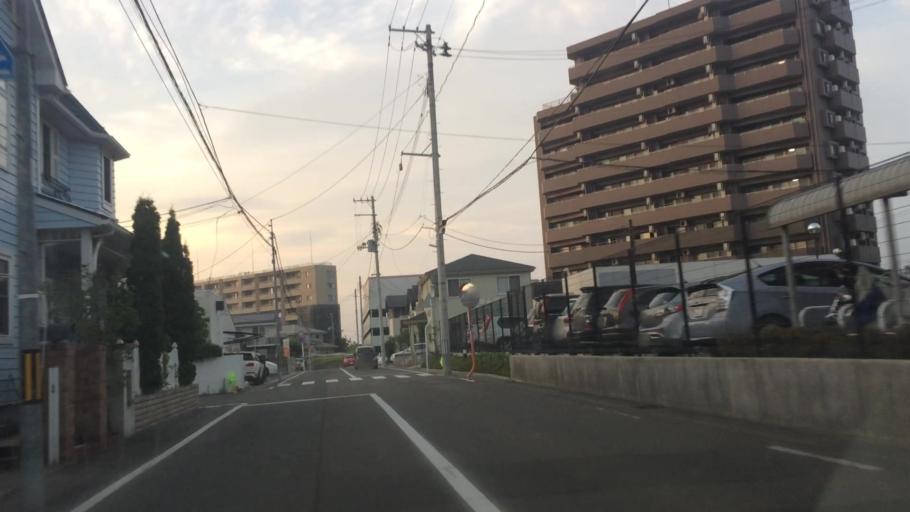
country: JP
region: Miyagi
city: Sendai-shi
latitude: 38.2988
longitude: 140.8979
